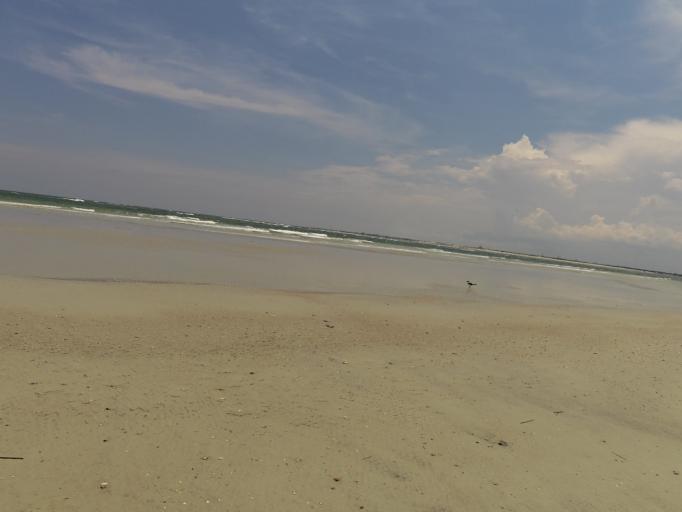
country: US
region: Florida
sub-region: Duval County
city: Atlantic Beach
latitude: 30.4338
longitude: -81.4063
